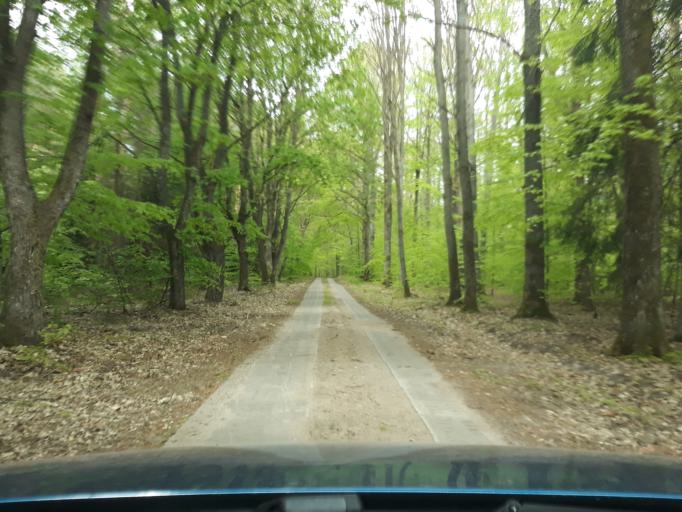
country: PL
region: Pomeranian Voivodeship
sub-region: Powiat czluchowski
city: Czluchow
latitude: 53.7538
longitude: 17.3353
